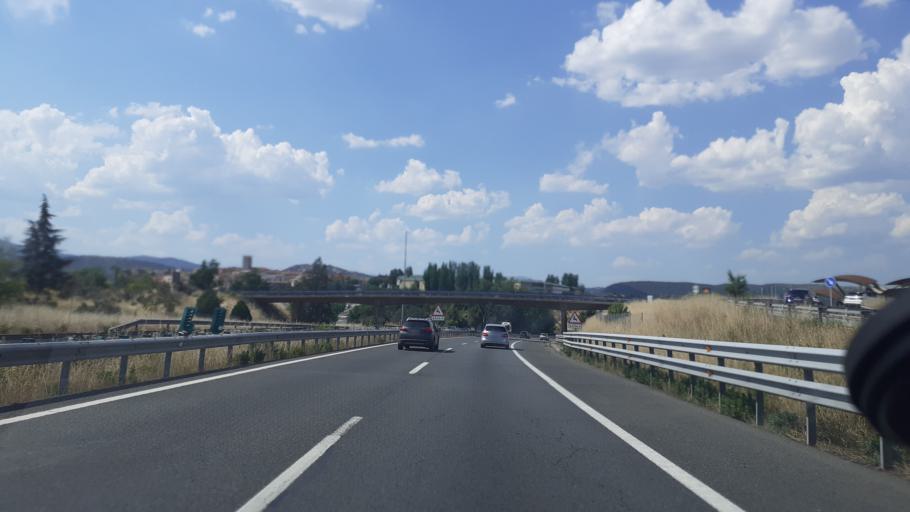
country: ES
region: Madrid
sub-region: Provincia de Madrid
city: San Agustin de Guadalix
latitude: 40.6719
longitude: -3.6109
